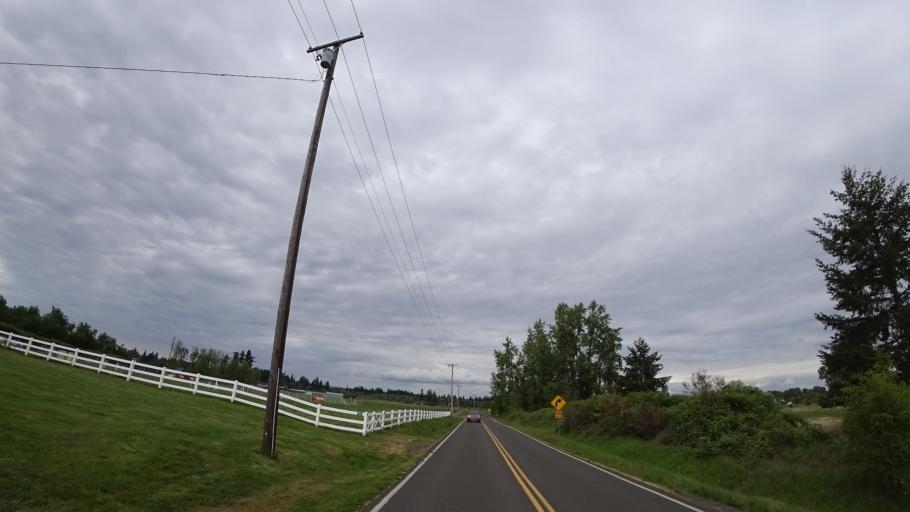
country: US
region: Oregon
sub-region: Washington County
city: Hillsboro
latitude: 45.4783
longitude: -122.9529
